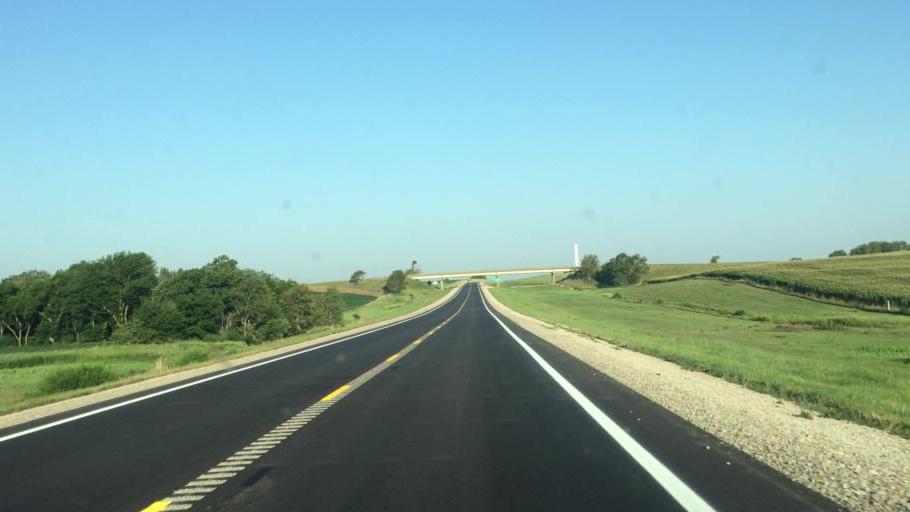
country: US
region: Kansas
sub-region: Doniphan County
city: Highland
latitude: 39.8421
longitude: -95.3347
